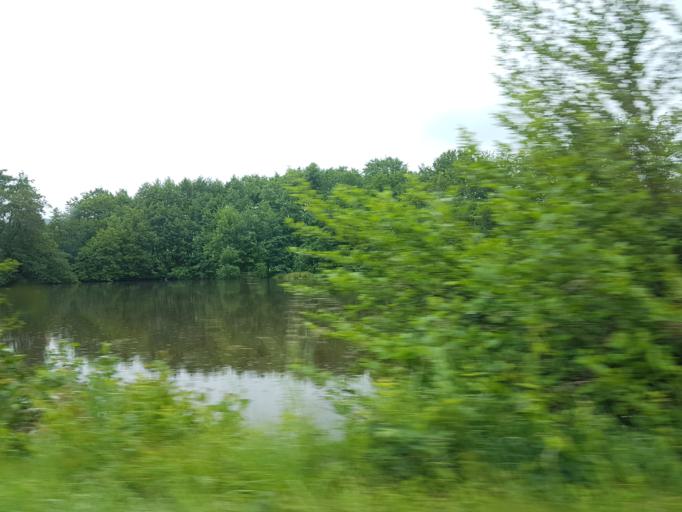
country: FR
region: Bourgogne
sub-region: Departement de la Nievre
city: Chateau-Chinon(Ville)
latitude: 47.1624
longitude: 3.8533
